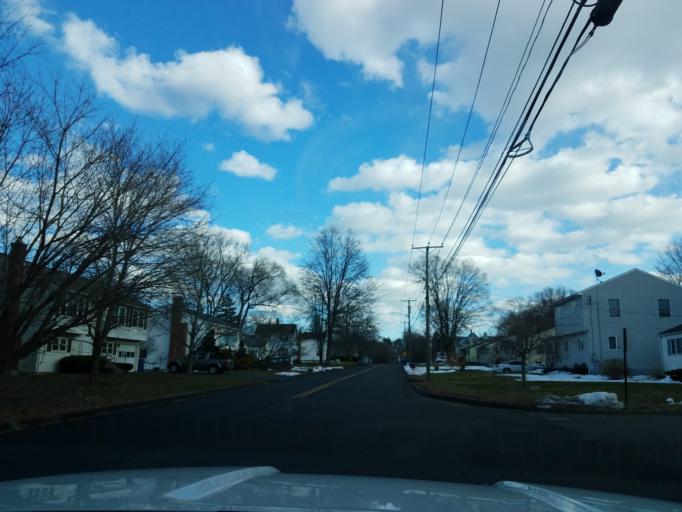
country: US
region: Connecticut
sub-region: Hartford County
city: Kensington
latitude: 41.6256
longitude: -72.7516
